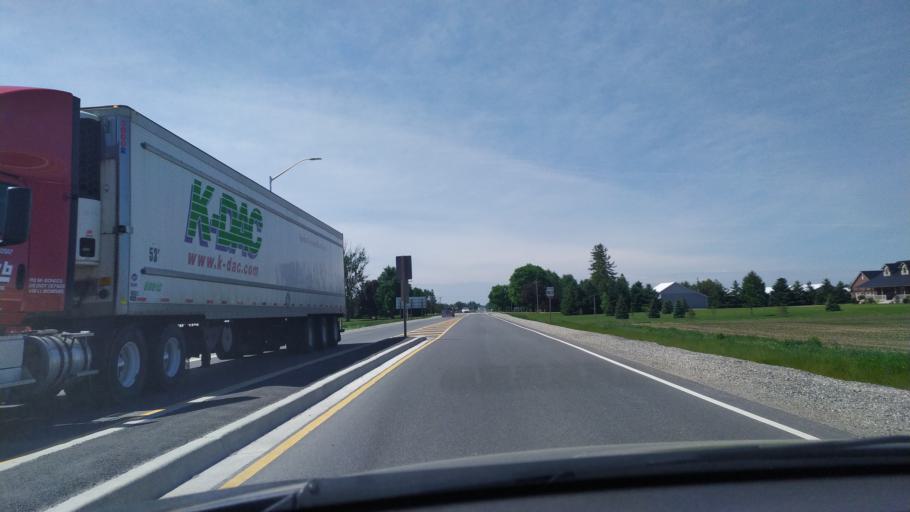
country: CA
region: Ontario
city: Stratford
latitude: 43.3232
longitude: -81.0235
